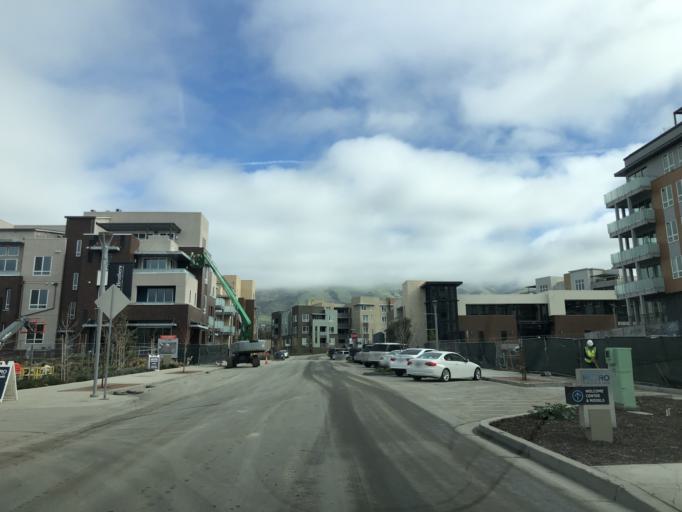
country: US
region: California
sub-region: Alameda County
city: Fremont
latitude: 37.5039
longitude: -121.9364
